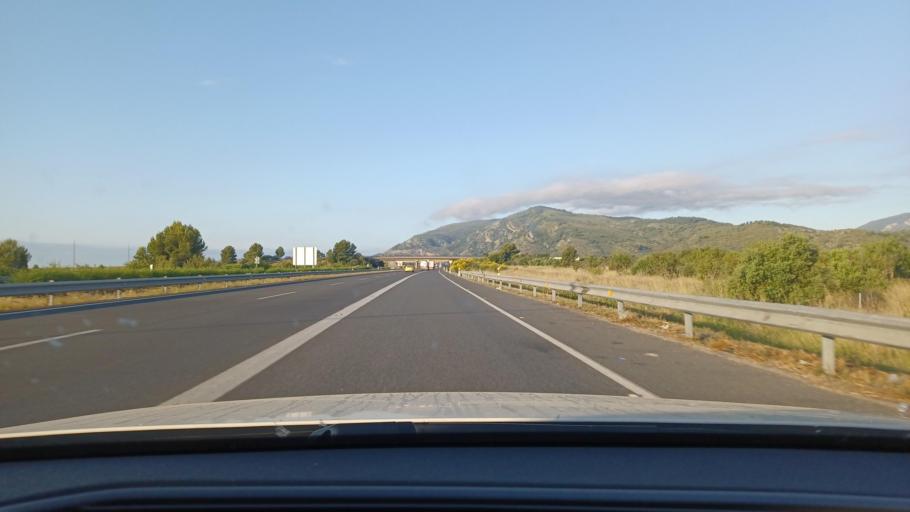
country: ES
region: Valencia
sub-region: Provincia de Castello
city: Orpesa/Oropesa del Mar
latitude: 40.1310
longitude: 0.1389
